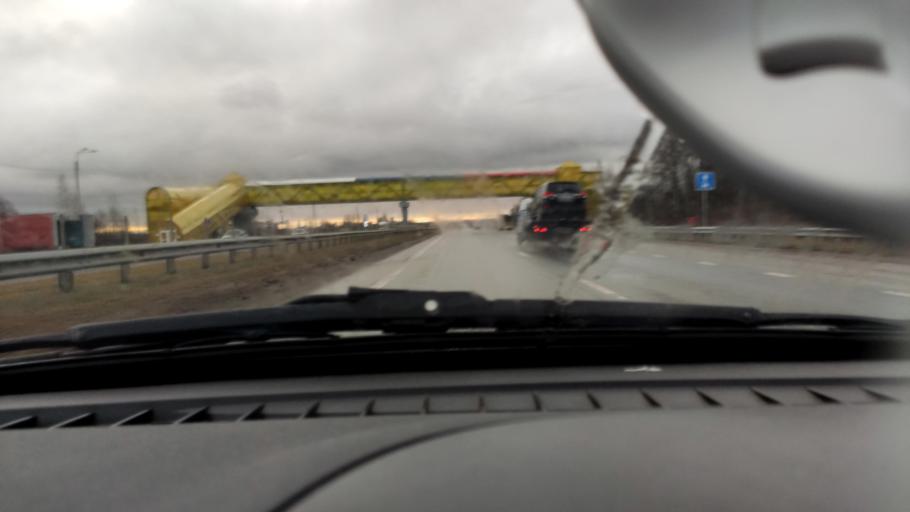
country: RU
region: Perm
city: Froly
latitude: 57.9096
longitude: 56.2650
